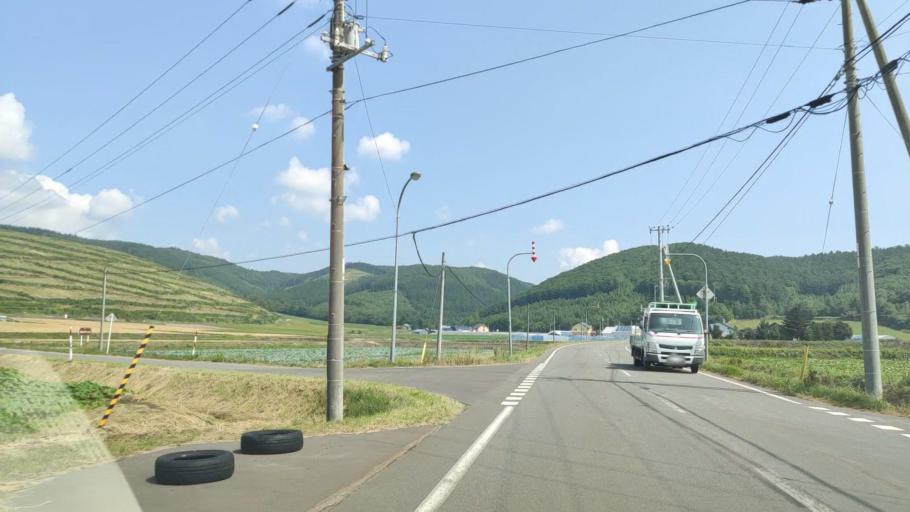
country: JP
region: Hokkaido
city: Shimo-furano
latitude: 43.4154
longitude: 142.3997
